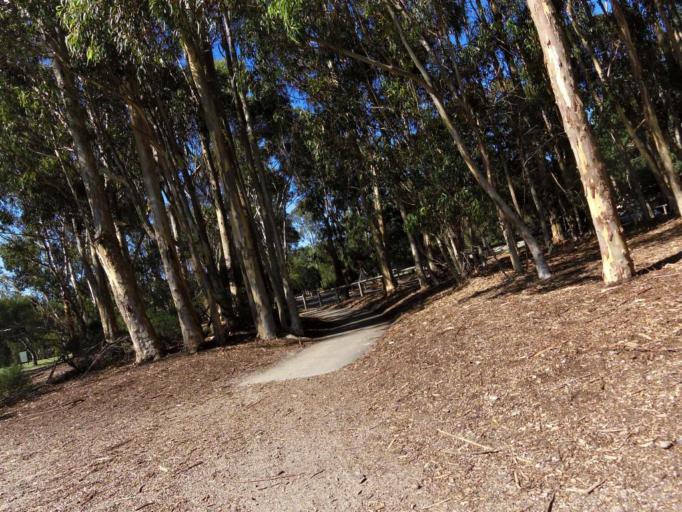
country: AU
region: Victoria
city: Ivanhoe East
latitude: -37.7876
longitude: 145.0597
